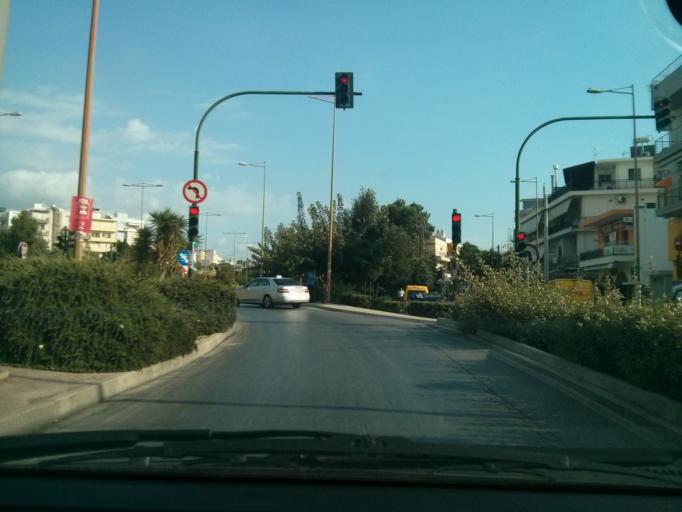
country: GR
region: Crete
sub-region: Nomos Irakleiou
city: Irakleion
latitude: 35.3263
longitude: 25.1384
